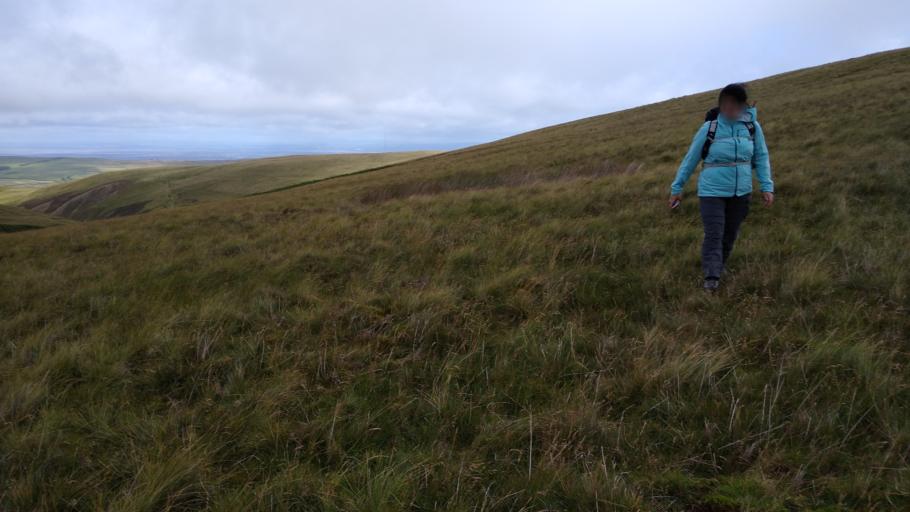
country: GB
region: England
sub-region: Cumbria
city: Keswick
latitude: 54.7081
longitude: -3.0684
